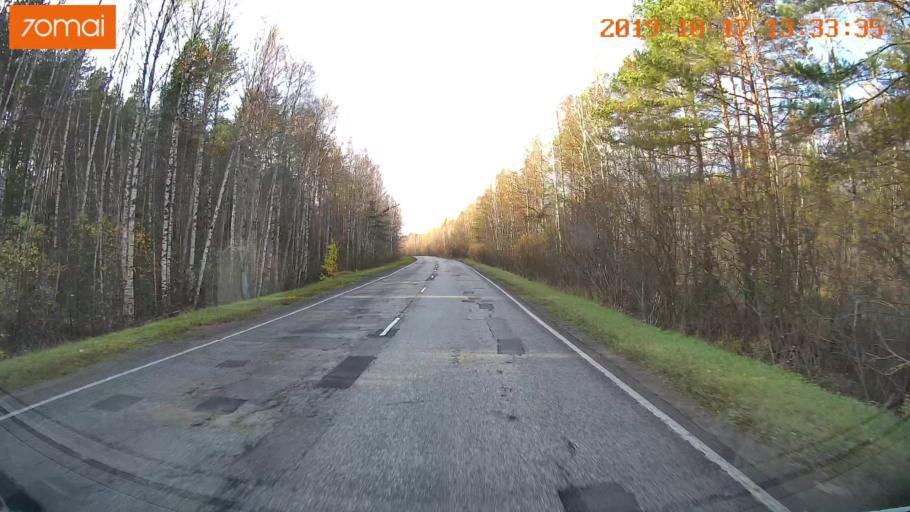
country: RU
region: Vladimir
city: Velikodvorskiy
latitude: 55.1433
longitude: 40.7380
